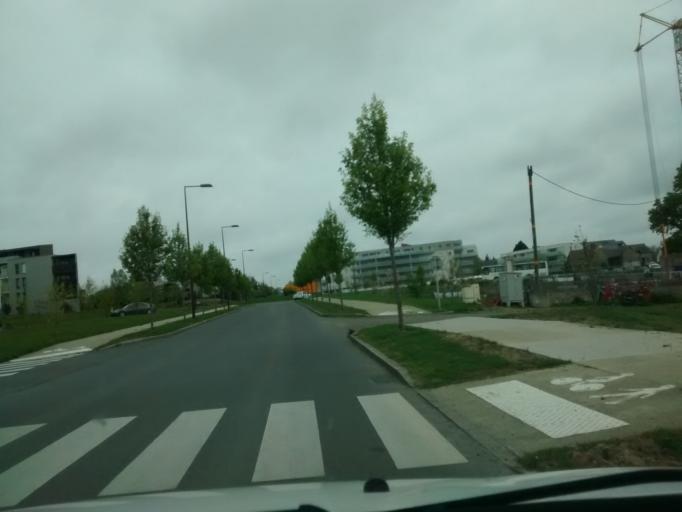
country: FR
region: Brittany
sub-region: Departement d'Ille-et-Vilaine
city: Fouillard
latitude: 48.1501
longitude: -1.5785
